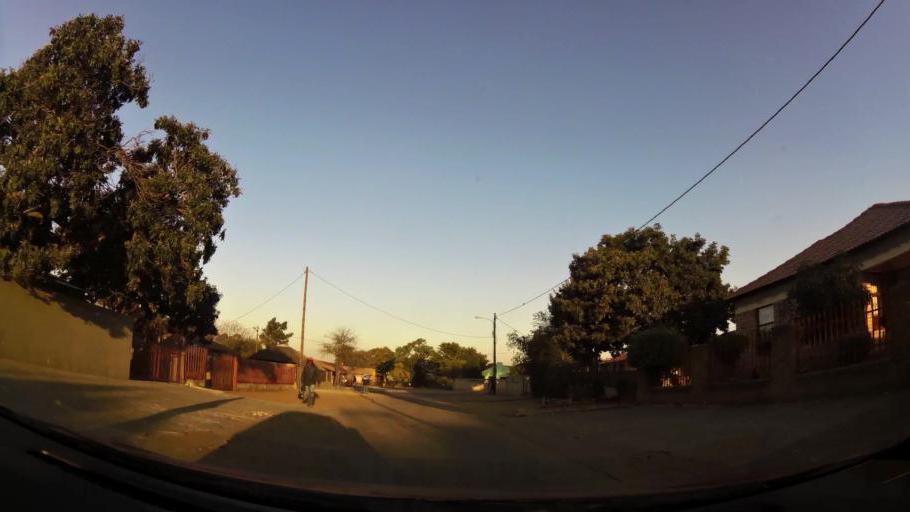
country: ZA
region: North-West
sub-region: Bojanala Platinum District Municipality
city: Rustenburg
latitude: -25.6460
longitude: 27.2160
